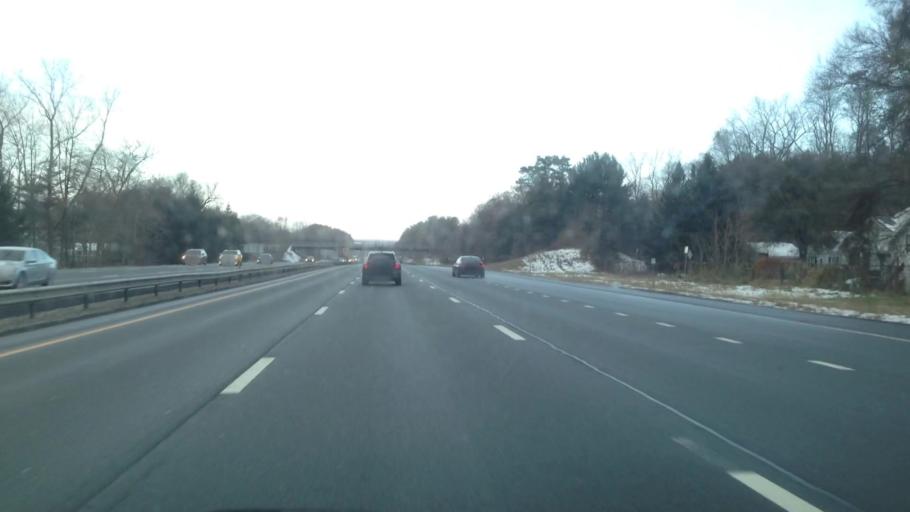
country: US
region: New York
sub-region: Schenectady County
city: Rotterdam
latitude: 42.7569
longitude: -73.9392
